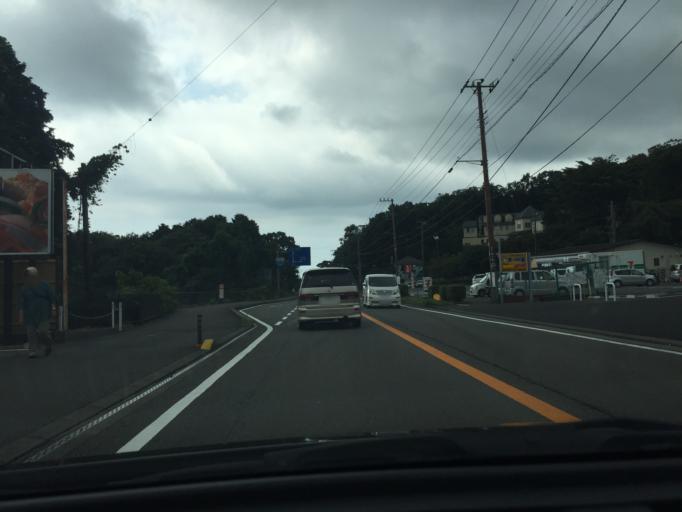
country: JP
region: Shizuoka
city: Ito
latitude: 34.9120
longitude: 139.1199
